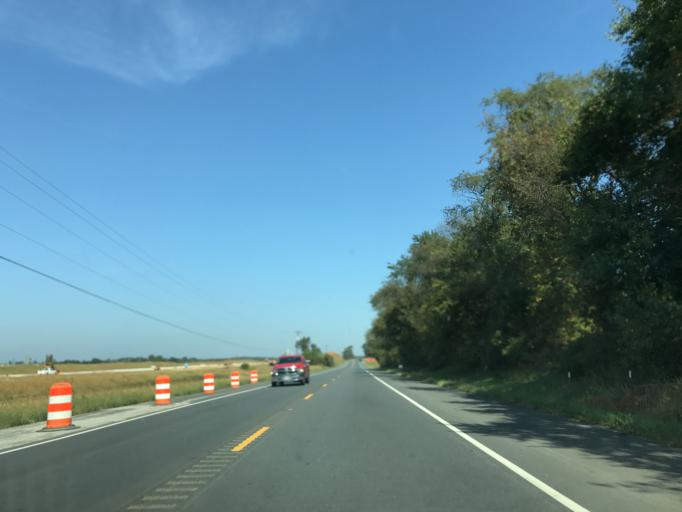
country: US
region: Delaware
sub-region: New Castle County
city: Middletown
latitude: 39.4284
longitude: -75.7606
